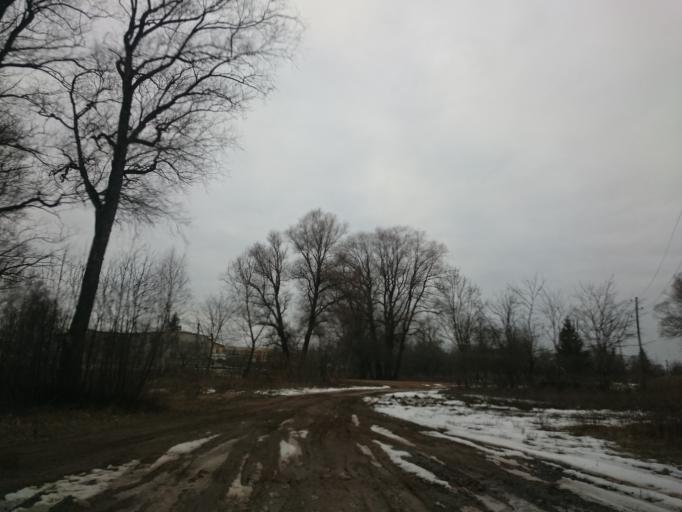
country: LV
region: Adazi
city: Adazi
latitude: 57.0811
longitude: 24.3300
